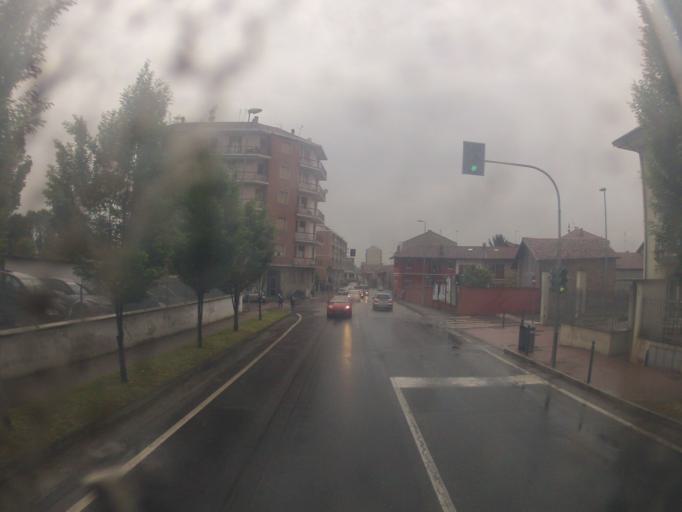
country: IT
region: Piedmont
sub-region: Provincia di Torino
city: La Loggia
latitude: 44.9533
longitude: 7.6685
